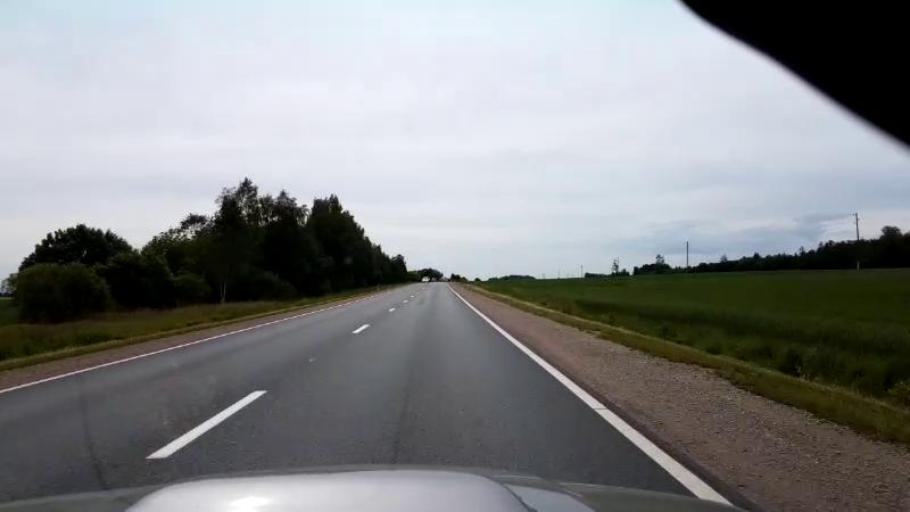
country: LV
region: Bauskas Rajons
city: Bauska
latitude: 56.4882
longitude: 24.1771
